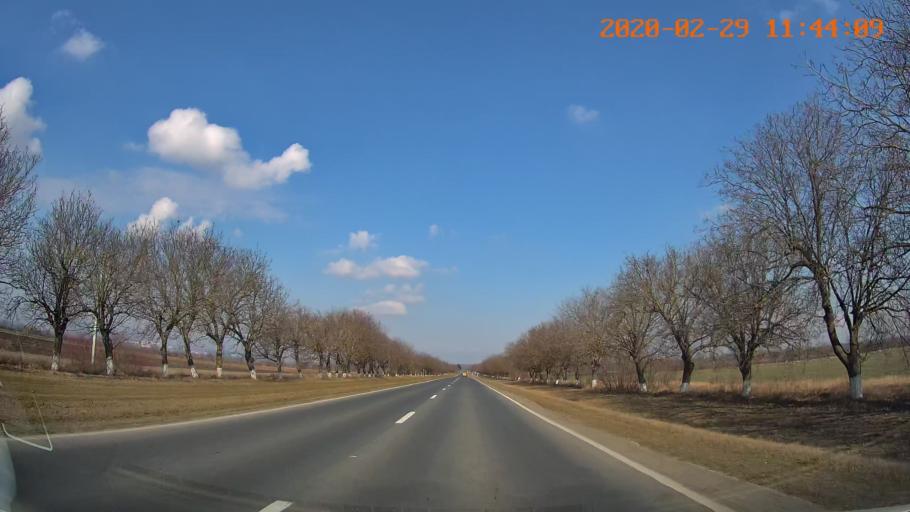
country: MD
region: Rezina
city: Saharna
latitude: 47.7071
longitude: 29.0010
